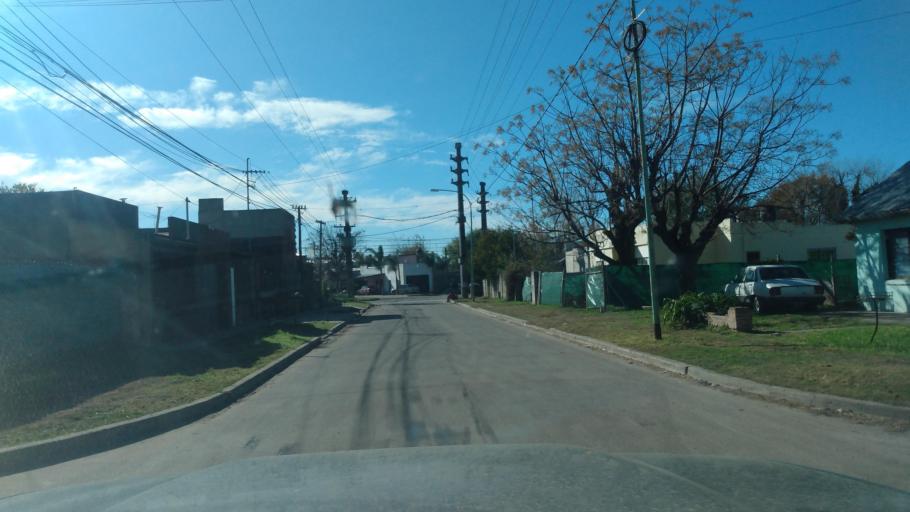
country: AR
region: Buenos Aires
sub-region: Partido de Lujan
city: Lujan
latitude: -34.5634
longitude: -59.0894
